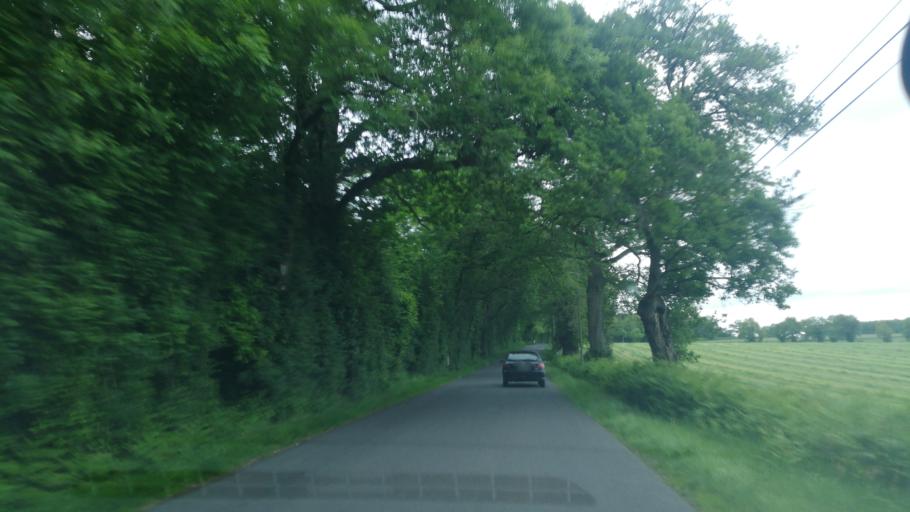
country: FR
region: Poitou-Charentes
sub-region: Departement des Deux-Sevres
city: Boisme
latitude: 46.7864
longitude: -0.4317
